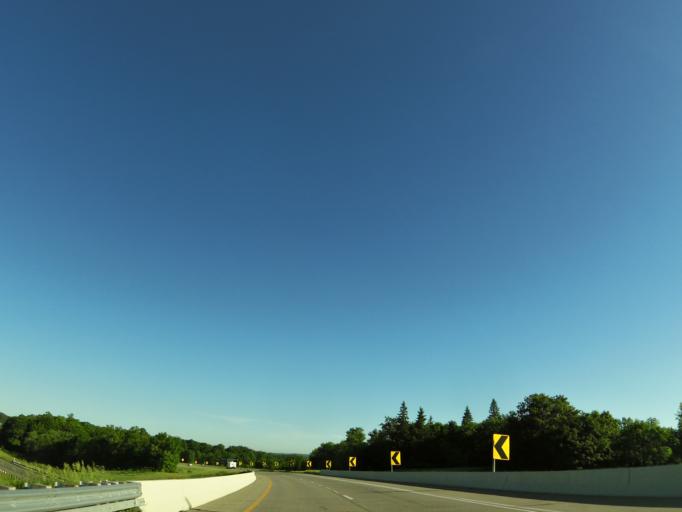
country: US
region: Minnesota
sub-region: Stearns County
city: Collegeville
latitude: 45.5824
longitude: -94.3582
